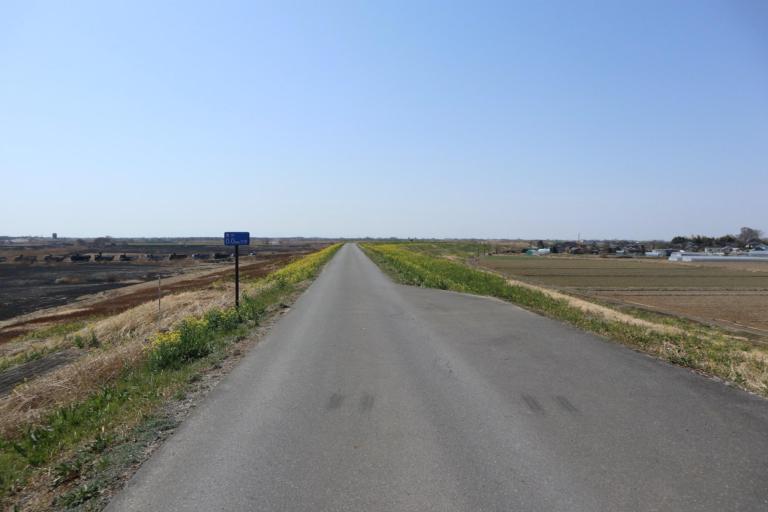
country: JP
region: Ibaraki
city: Koga
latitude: 36.2405
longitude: 139.7133
